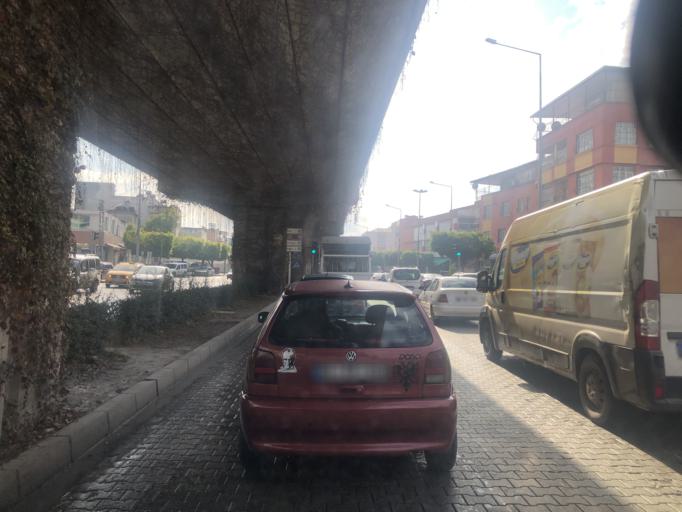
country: TR
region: Adana
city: Seyhan
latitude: 36.9830
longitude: 35.3204
